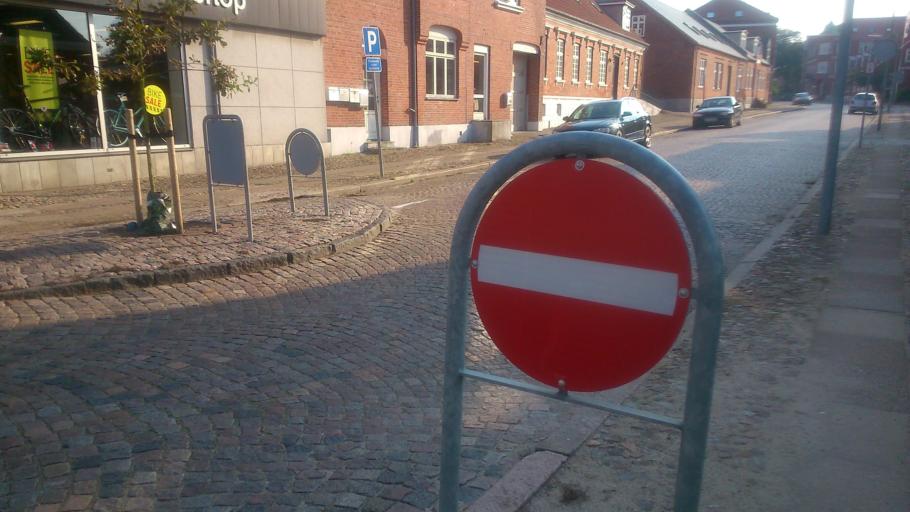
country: DK
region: Central Jutland
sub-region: Ringkobing-Skjern Kommune
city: Ringkobing
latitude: 56.0928
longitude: 8.2495
